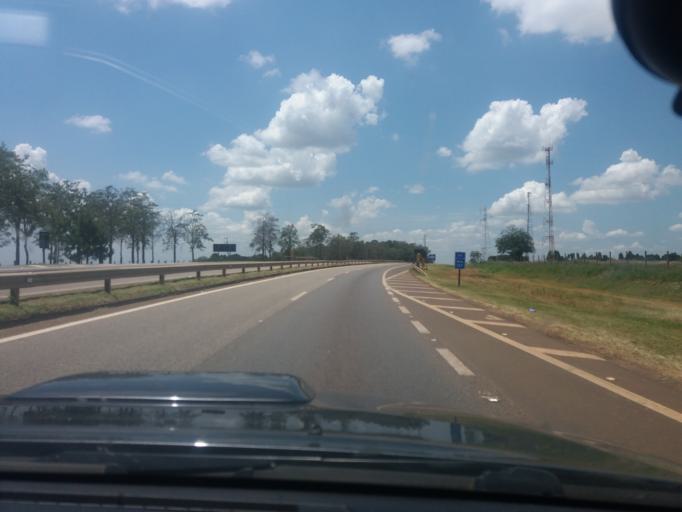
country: BR
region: Sao Paulo
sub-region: Itapetininga
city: Itapetininga
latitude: -23.4932
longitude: -47.9681
